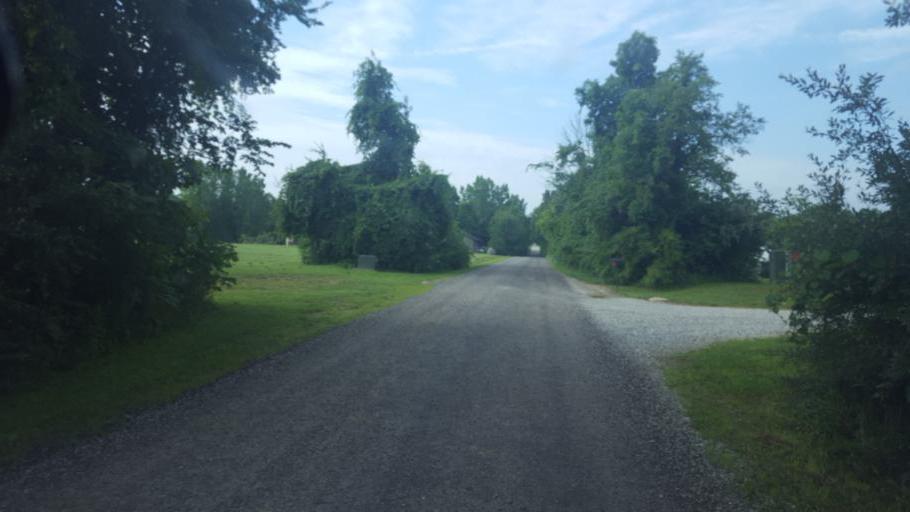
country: US
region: Ohio
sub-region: Delaware County
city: Ashley
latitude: 40.3683
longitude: -82.8840
